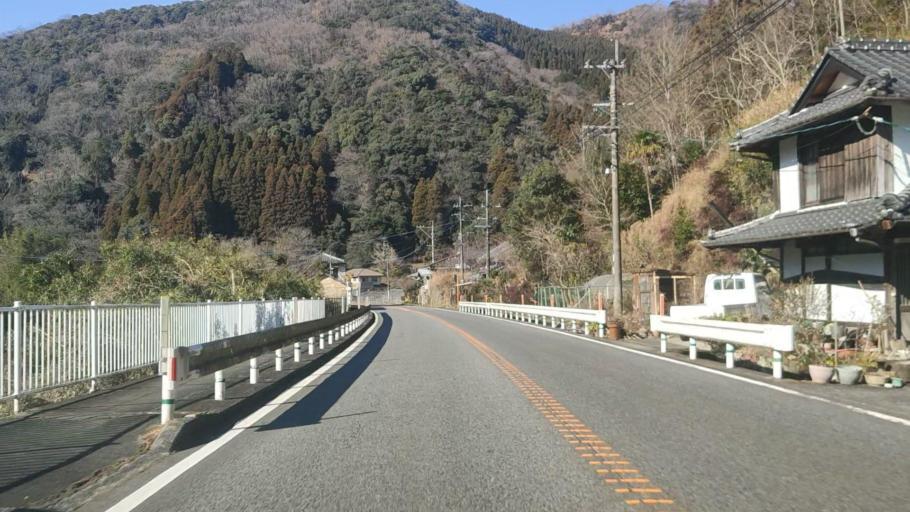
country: JP
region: Oita
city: Usuki
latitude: 33.0060
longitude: 131.7415
